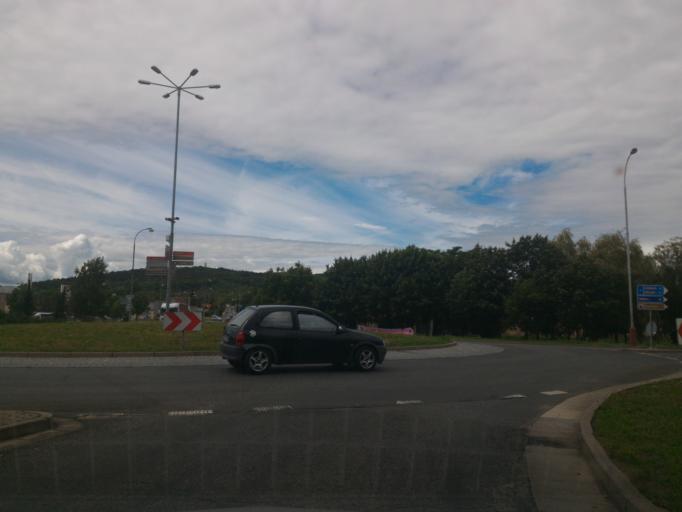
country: CZ
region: Central Bohemia
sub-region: Okres Kutna Hora
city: Kutna Hora
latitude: 49.9594
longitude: 15.2854
